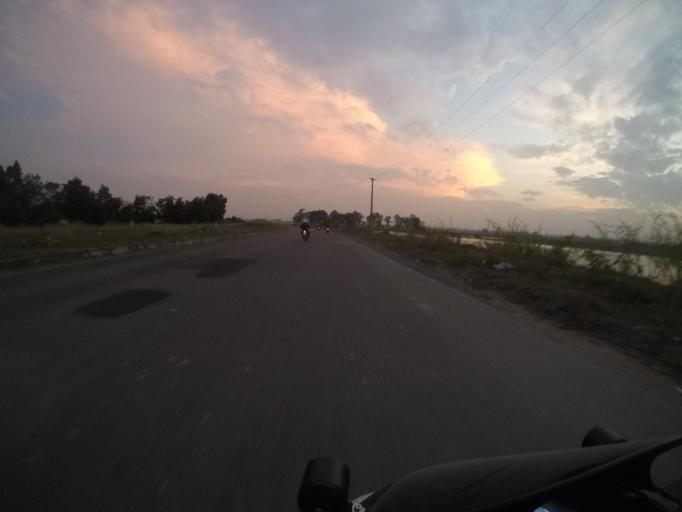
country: VN
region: Vinh Phuc
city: Phuc Yen
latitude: 21.2525
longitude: 105.7216
